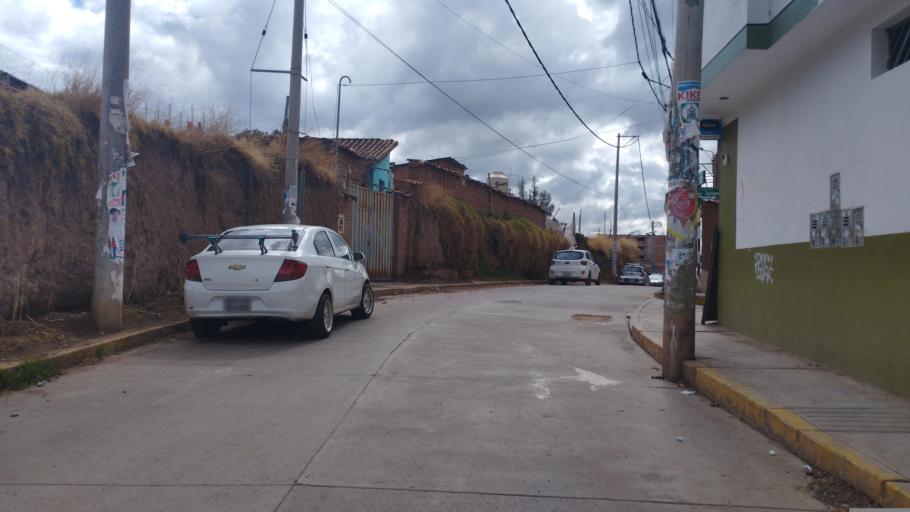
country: PE
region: Cusco
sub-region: Provincia de Cusco
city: Cusco
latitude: -13.5249
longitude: -71.9396
